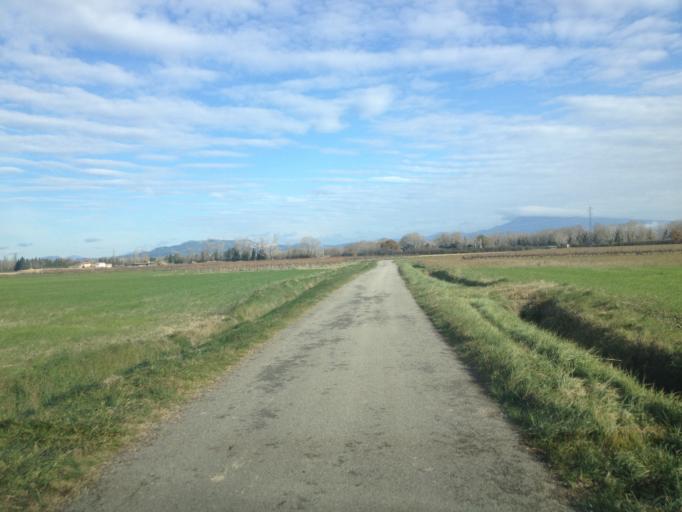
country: FR
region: Provence-Alpes-Cote d'Azur
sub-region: Departement du Vaucluse
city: Bedarrides
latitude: 44.0528
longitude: 4.9212
